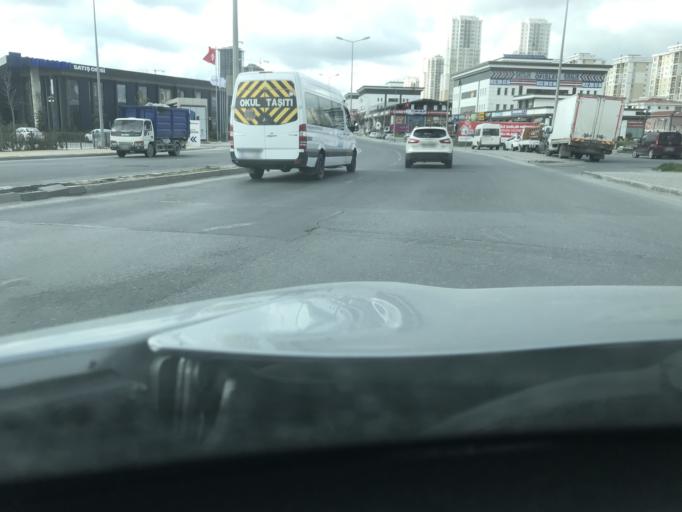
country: TR
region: Istanbul
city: Esenyurt
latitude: 41.0859
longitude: 28.6519
